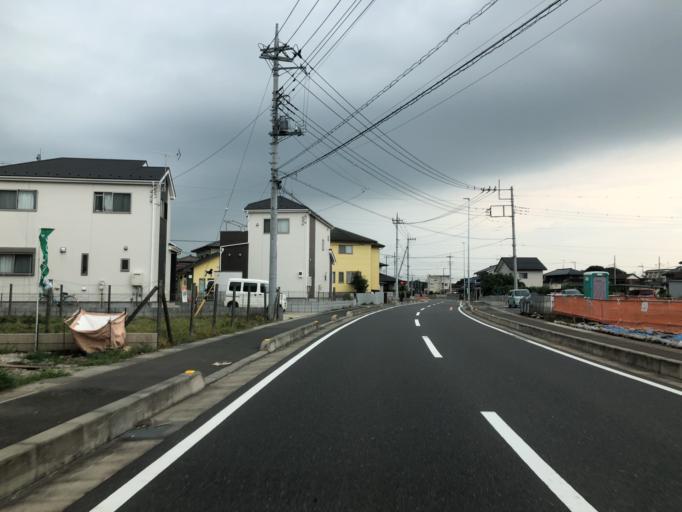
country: JP
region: Saitama
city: Sakado
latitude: 36.0064
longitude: 139.4016
